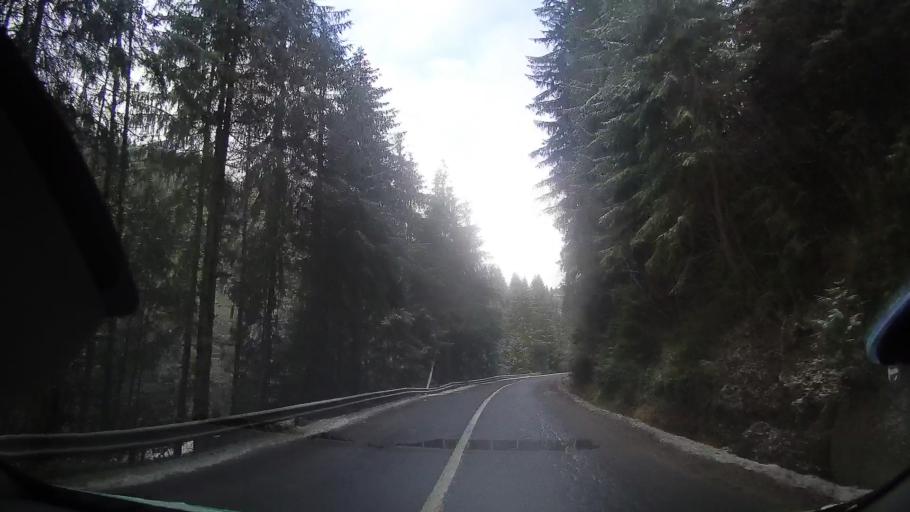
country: RO
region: Alba
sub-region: Comuna Horea
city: Horea
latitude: 46.4895
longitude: 22.9616
